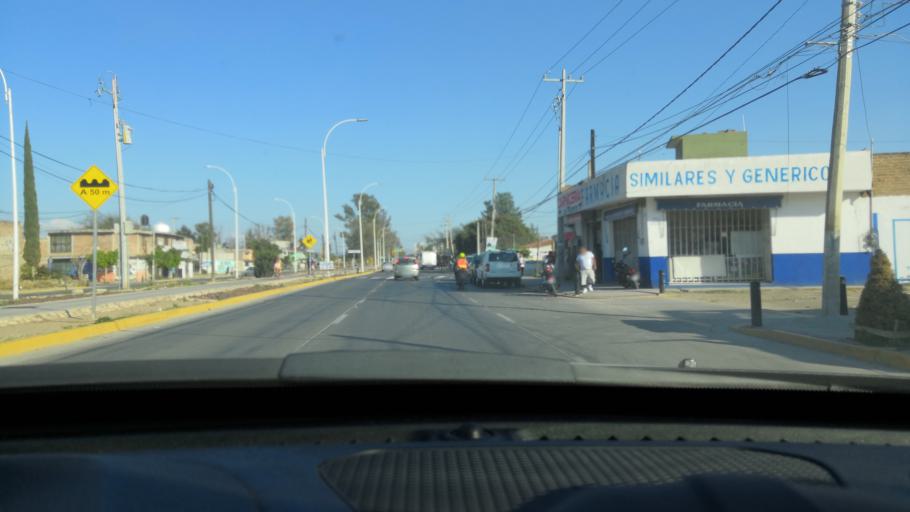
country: MX
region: Guanajuato
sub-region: Leon
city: San Jose de Duran (Los Troncoso)
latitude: 21.0617
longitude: -101.6199
